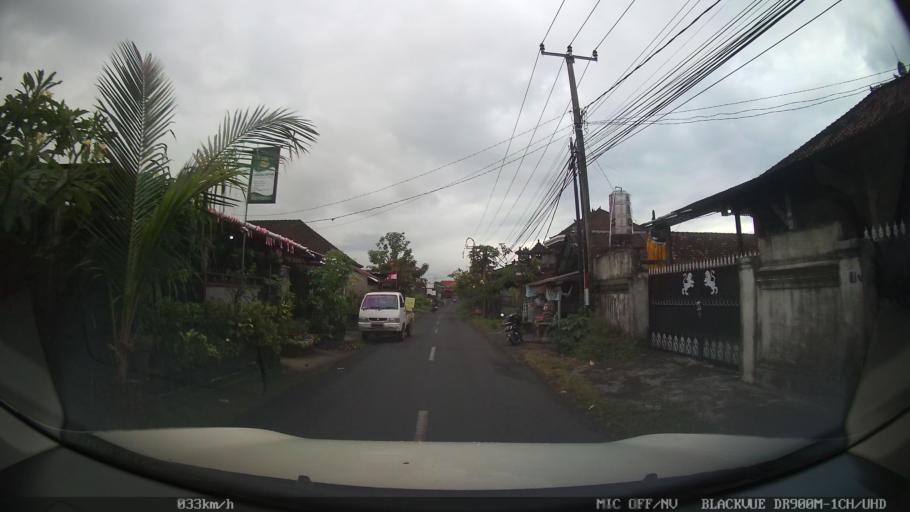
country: ID
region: Bali
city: Banjar Pasekan
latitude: -8.6156
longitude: 115.2772
